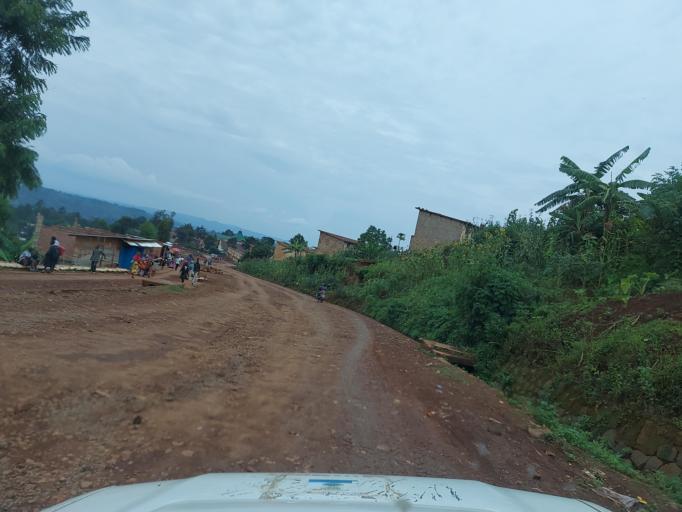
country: CD
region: South Kivu
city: Bukavu
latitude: -2.4788
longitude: 28.8223
